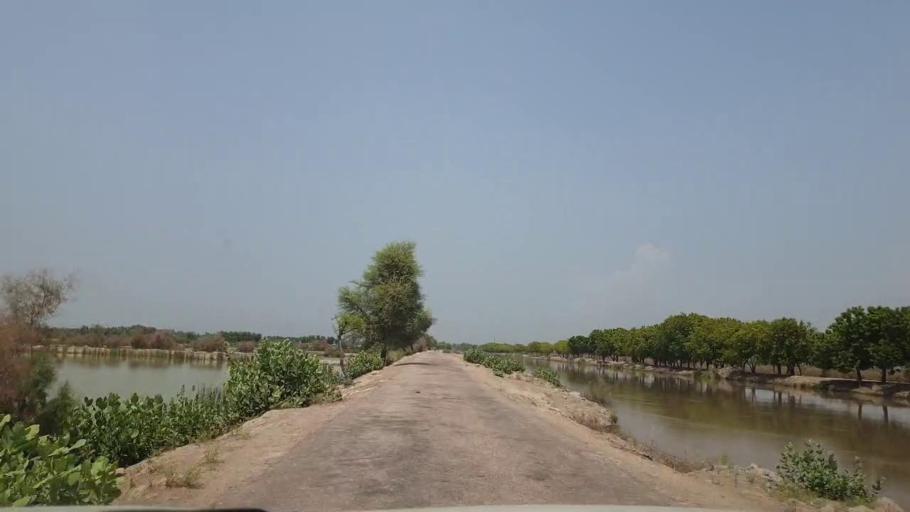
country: PK
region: Sindh
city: Dokri
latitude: 27.3475
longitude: 68.1119
